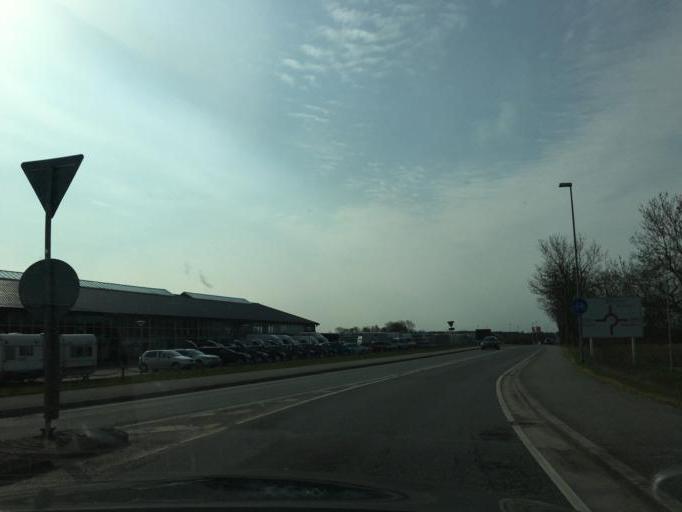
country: DK
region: South Denmark
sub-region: Vejen Kommune
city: Brorup
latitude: 55.5019
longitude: 9.0209
